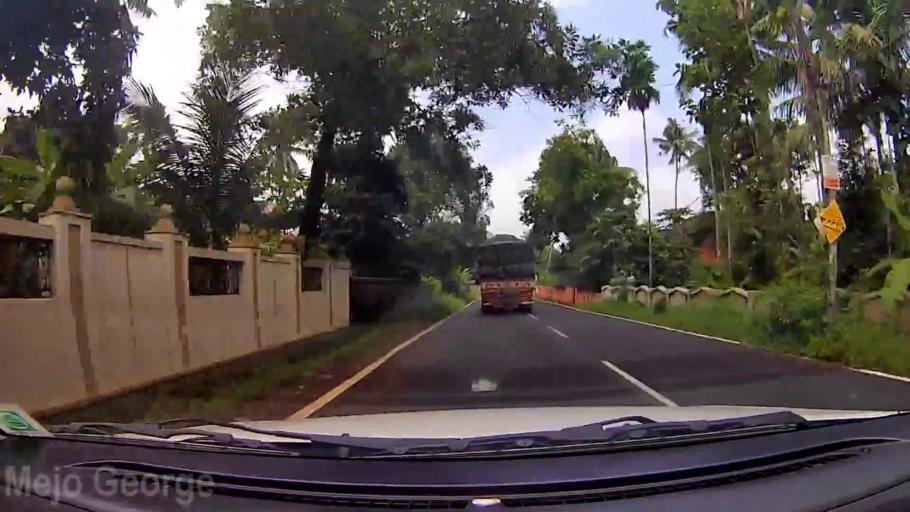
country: IN
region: Kerala
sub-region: Thrissur District
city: Kizhake Chalakudi
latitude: 10.3339
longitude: 76.3061
